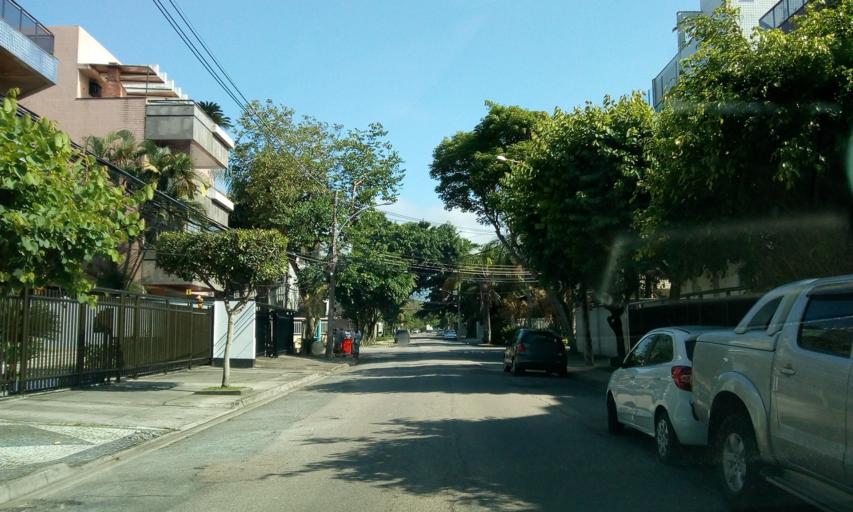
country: BR
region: Rio de Janeiro
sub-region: Nilopolis
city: Nilopolis
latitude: -23.0215
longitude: -43.4560
